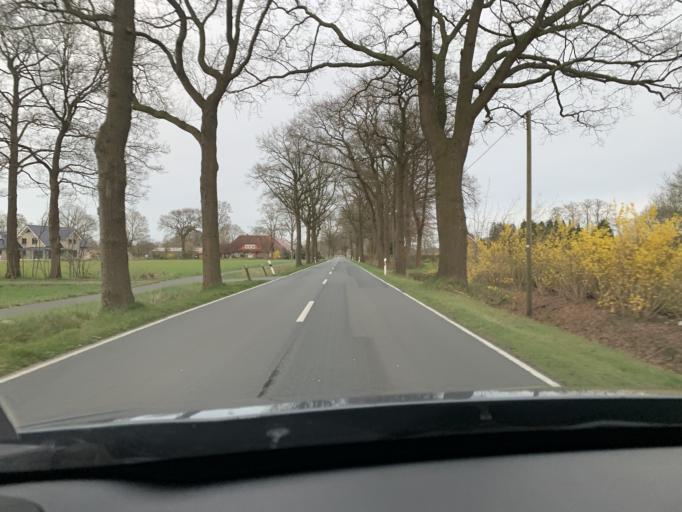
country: DE
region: Lower Saxony
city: Apen
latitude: 53.1775
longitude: 7.8025
